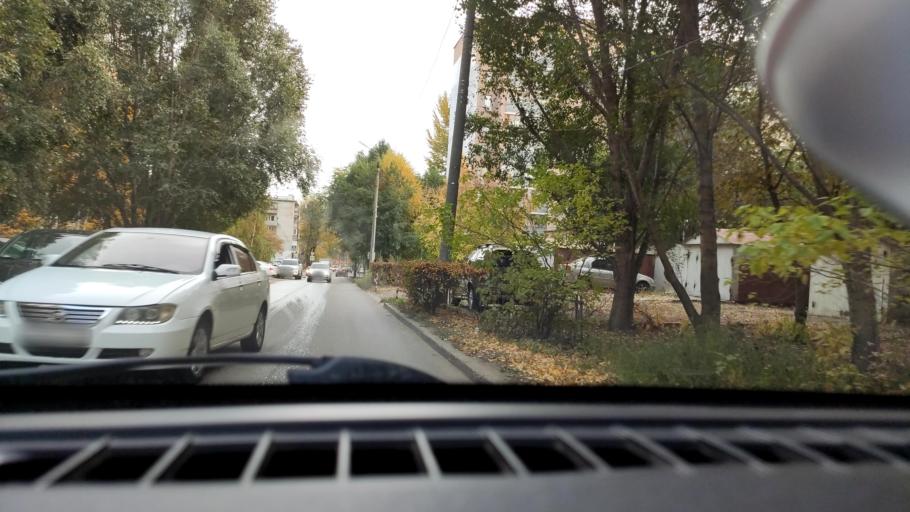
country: RU
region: Samara
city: Samara
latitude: 53.2319
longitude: 50.2503
